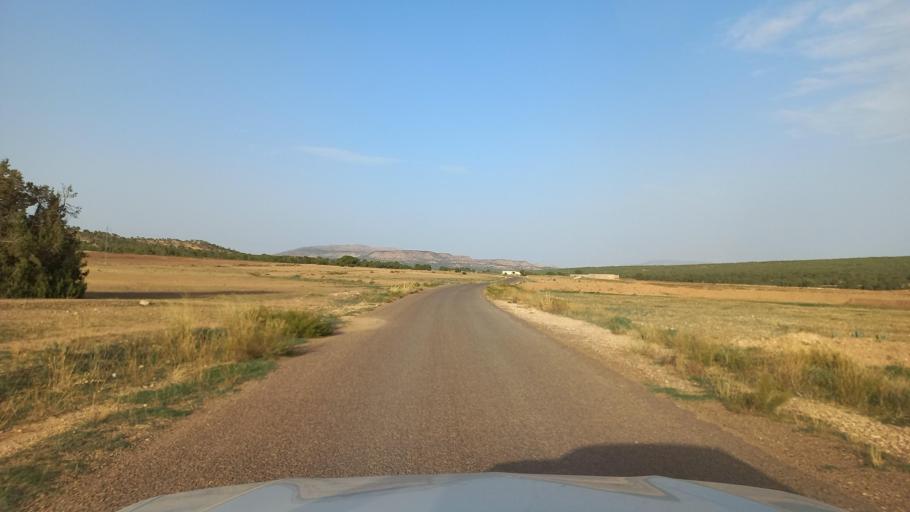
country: TN
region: Al Qasrayn
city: Kasserine
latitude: 35.3953
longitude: 8.8785
